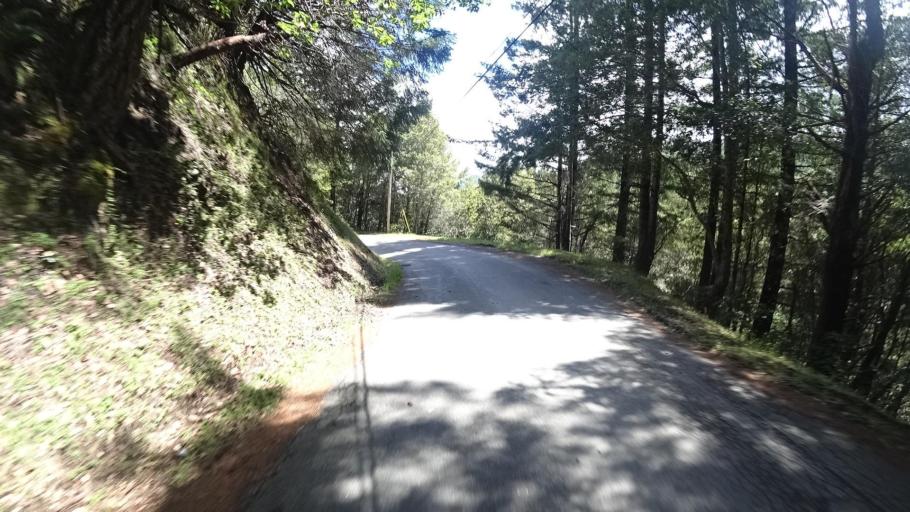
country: US
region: California
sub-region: Humboldt County
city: Blue Lake
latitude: 40.7612
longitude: -123.9518
